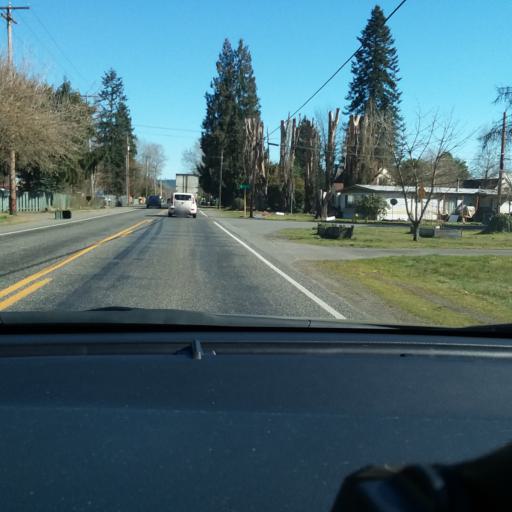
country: US
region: Washington
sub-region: Pierce County
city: North Puyallup
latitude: 47.2060
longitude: -122.2715
